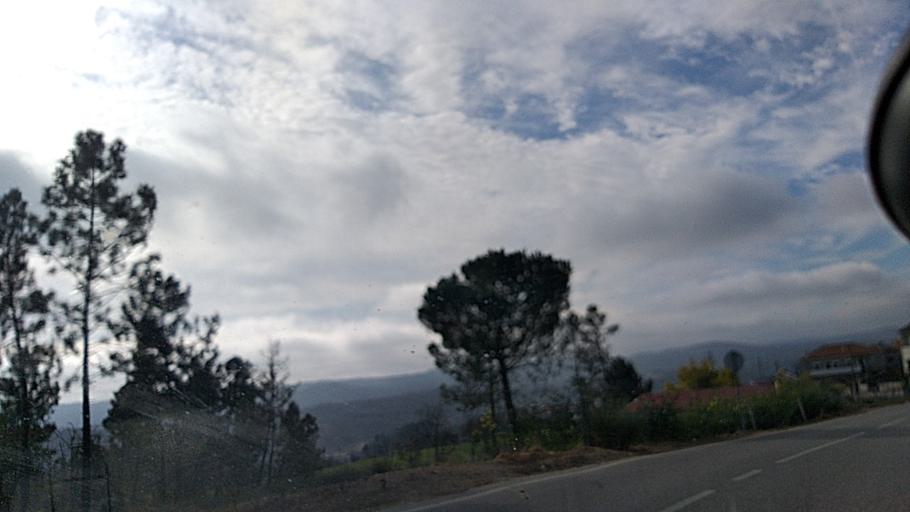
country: PT
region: Guarda
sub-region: Aguiar da Beira
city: Aguiar da Beira
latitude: 40.7410
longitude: -7.5545
